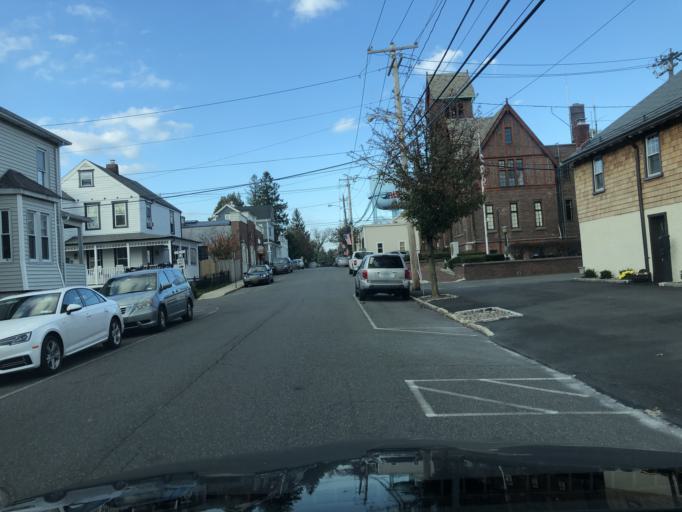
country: US
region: New York
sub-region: Nassau County
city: Sea Cliff
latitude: 40.8481
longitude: -73.6449
